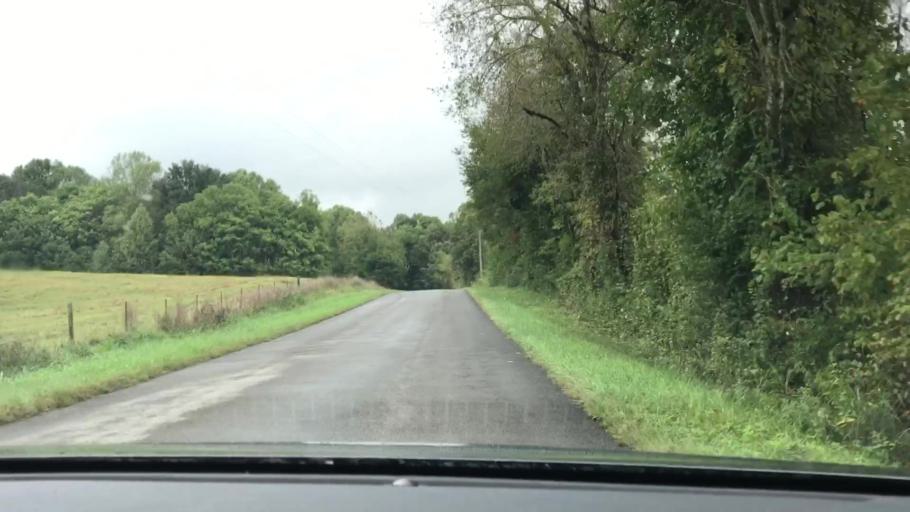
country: US
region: Kentucky
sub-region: Monroe County
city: Tompkinsville
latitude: 36.6186
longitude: -85.7709
